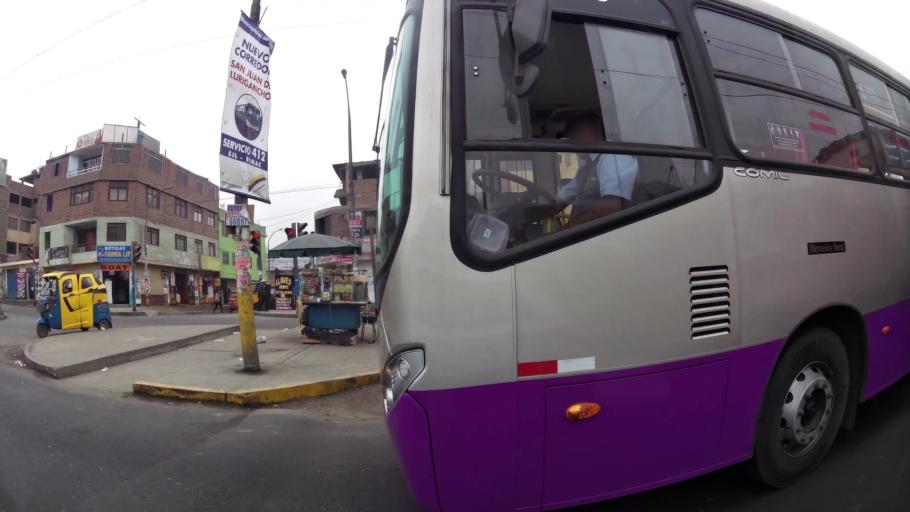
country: PE
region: Lima
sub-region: Lima
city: Urb. Santo Domingo
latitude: -11.9389
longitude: -76.9769
